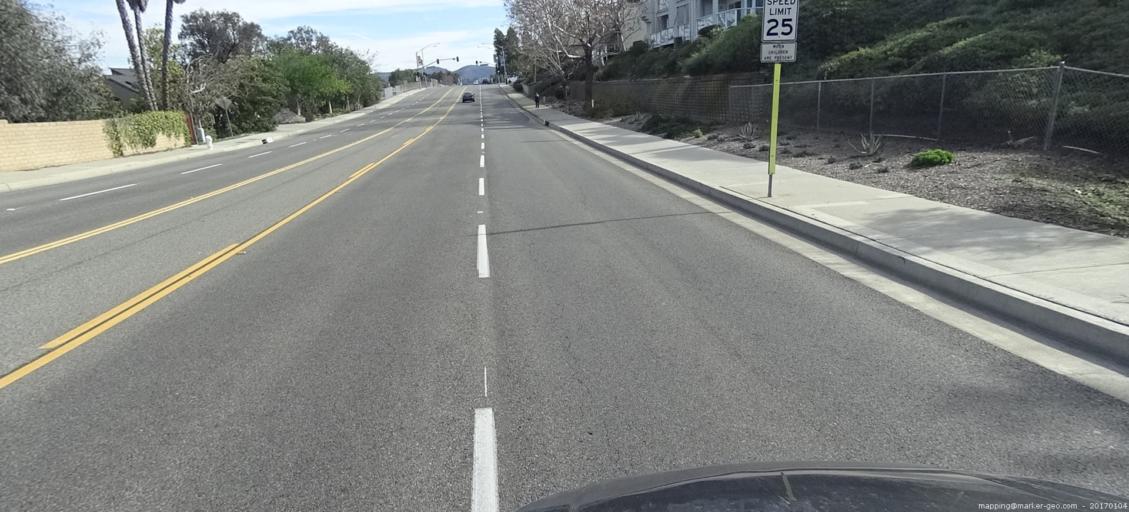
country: US
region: California
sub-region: Orange County
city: Dana Point
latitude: 33.4763
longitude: -117.7043
